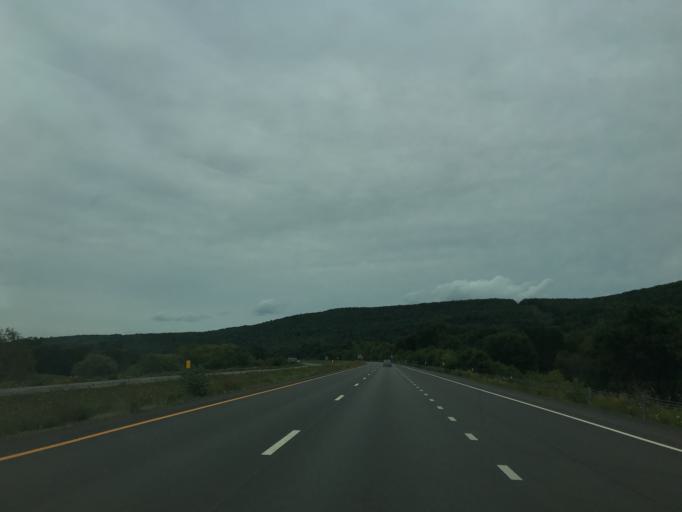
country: US
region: New York
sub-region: Delaware County
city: Sidney
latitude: 42.2931
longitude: -75.4004
